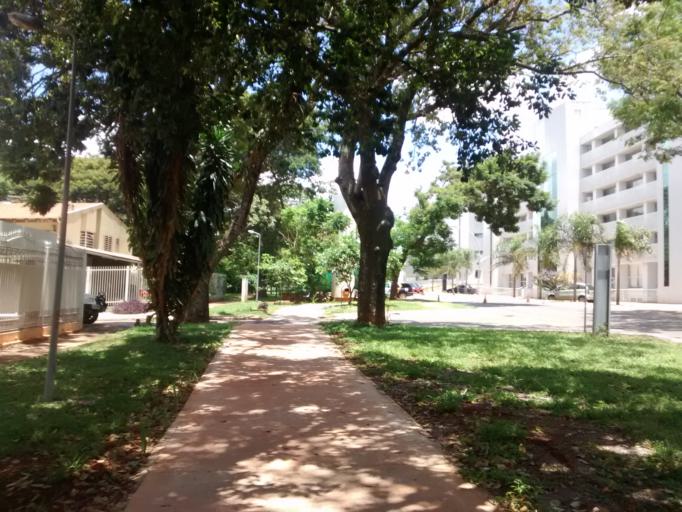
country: BR
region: Federal District
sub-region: Brasilia
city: Brasilia
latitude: -15.8194
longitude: -47.9202
